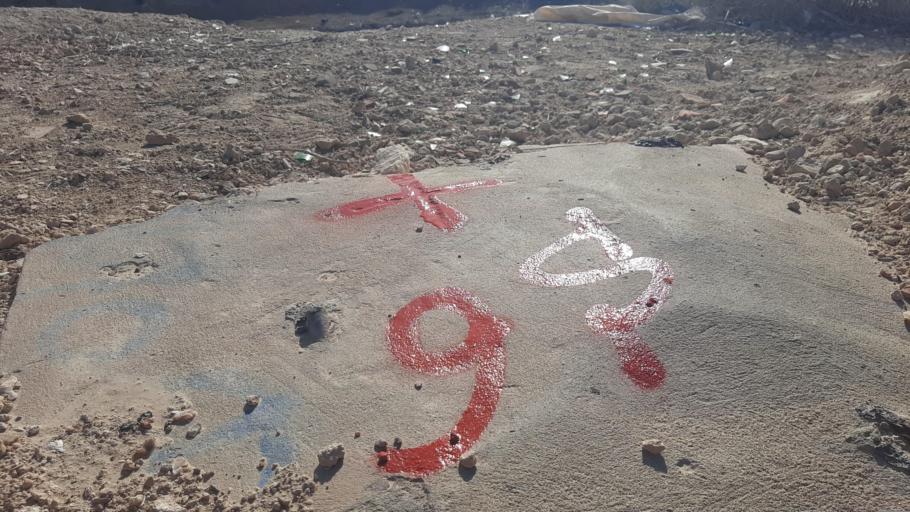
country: TN
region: Qabis
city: Gabes
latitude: 33.8730
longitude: 10.0902
